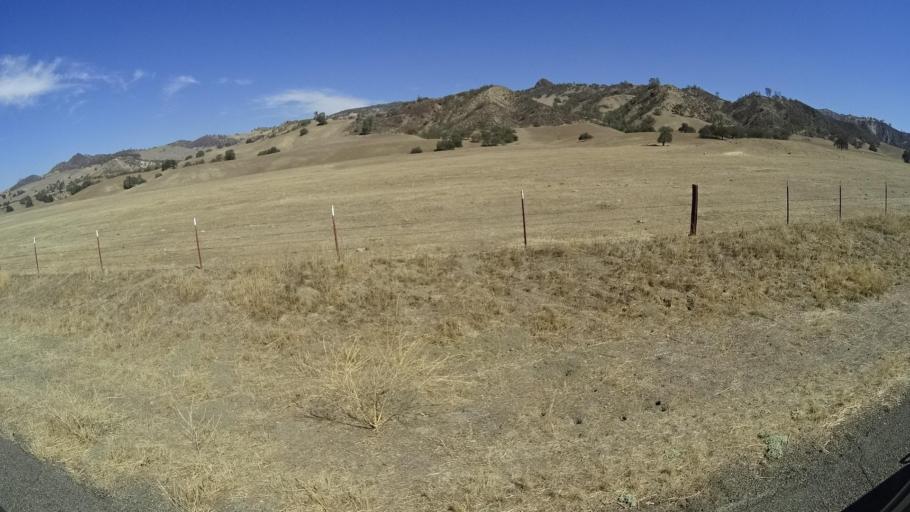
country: US
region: California
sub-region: Fresno County
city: Coalinga
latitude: 36.1078
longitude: -120.7145
